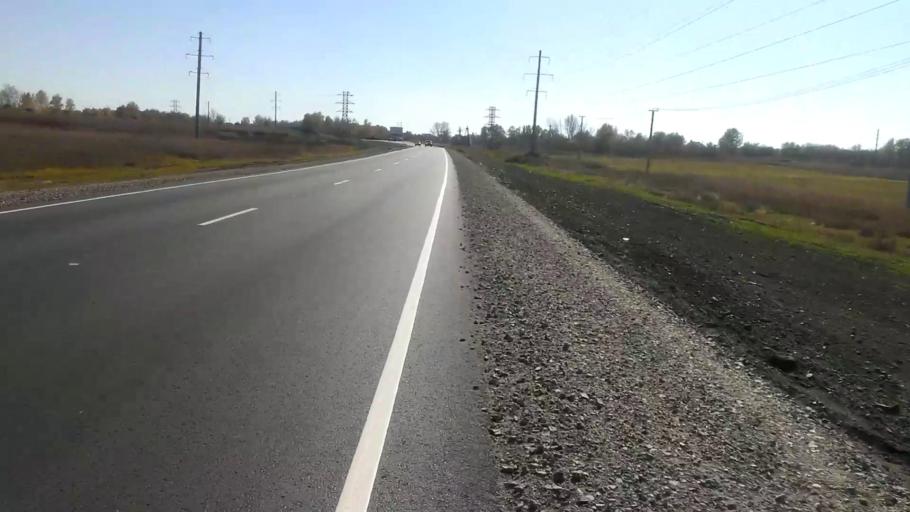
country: RU
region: Altai Krai
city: Sannikovo
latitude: 53.3322
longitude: 83.9380
